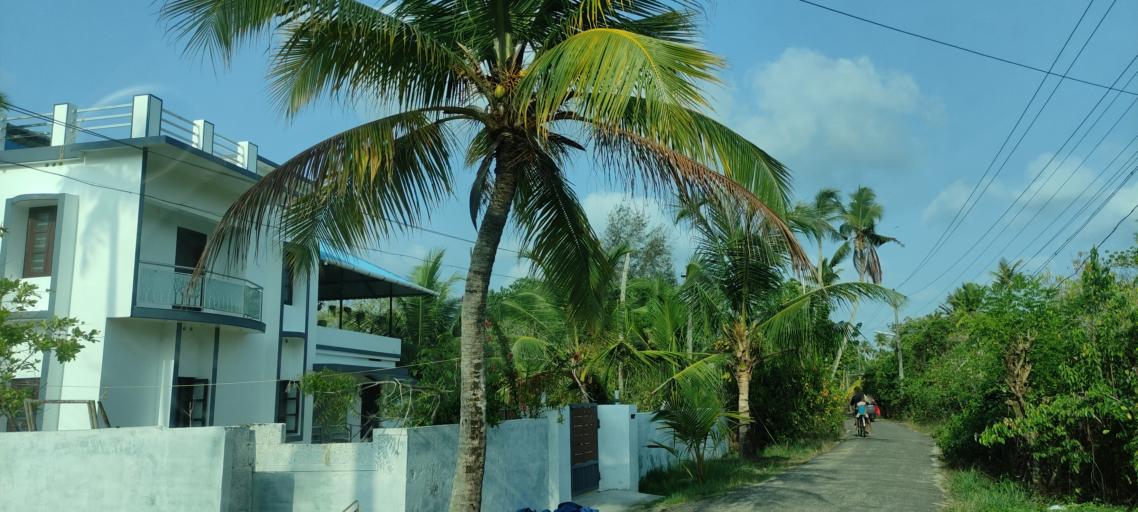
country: IN
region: Kerala
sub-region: Alappuzha
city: Vayalar
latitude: 9.7275
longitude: 76.2872
